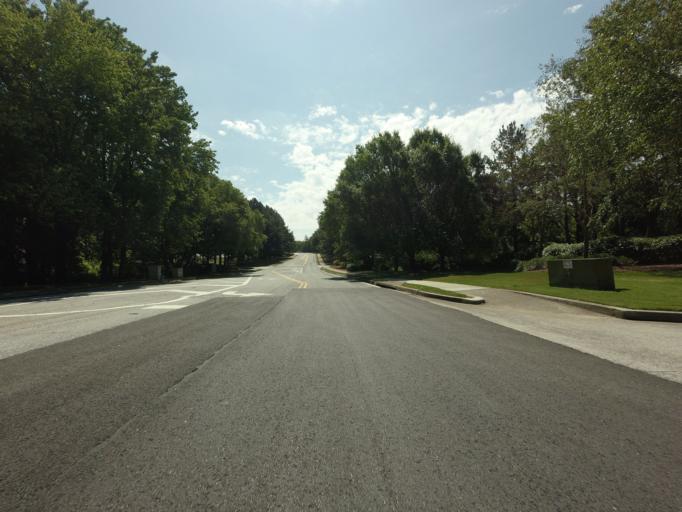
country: US
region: Georgia
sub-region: Fulton County
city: Johns Creek
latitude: 34.0637
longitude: -84.1684
